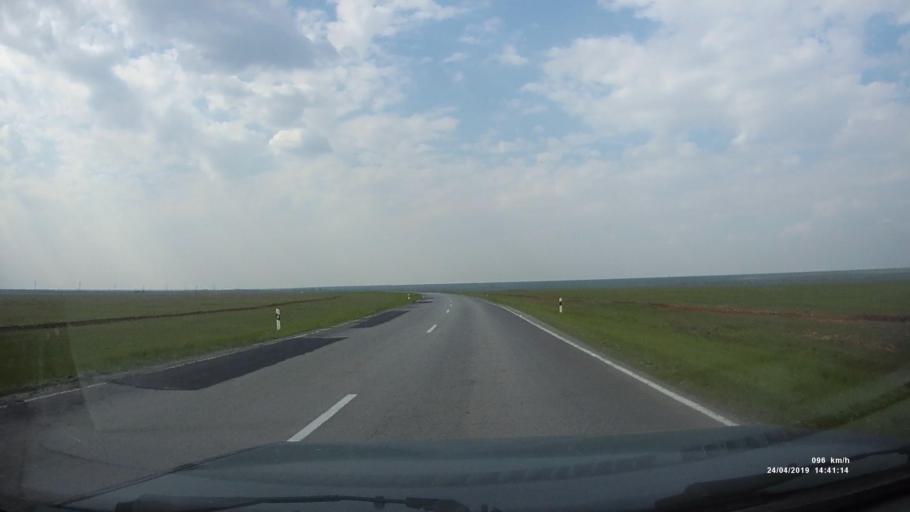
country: RU
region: Rostov
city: Remontnoye
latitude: 46.4429
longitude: 43.8823
